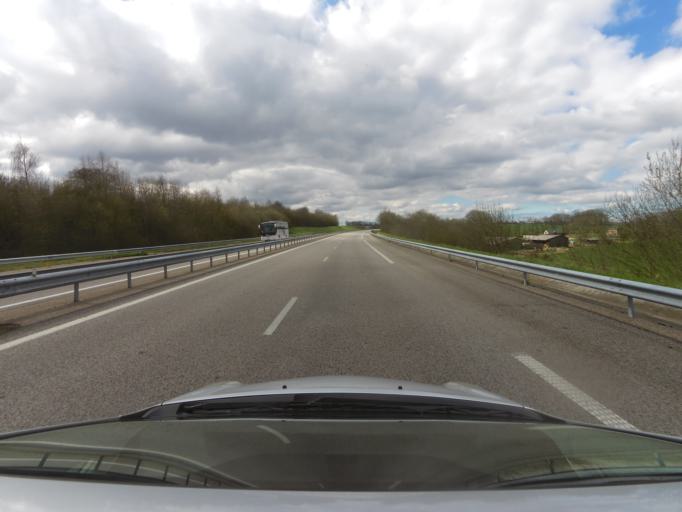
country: FR
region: Haute-Normandie
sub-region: Departement de la Seine-Maritime
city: Beuzeville-la-Grenier
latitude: 49.5700
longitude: 0.3976
